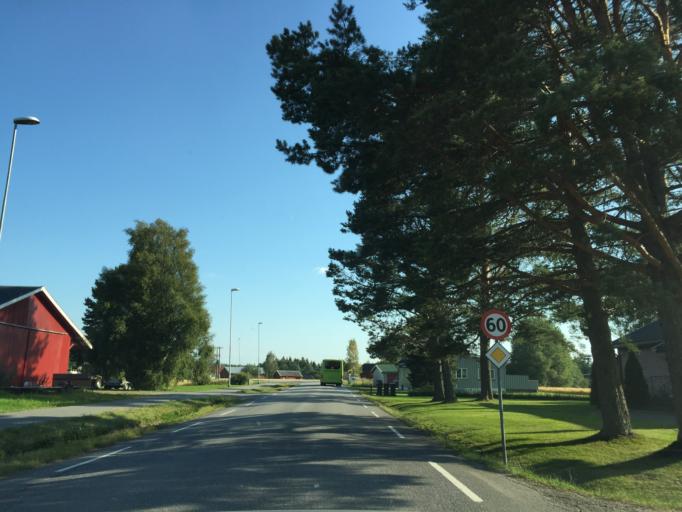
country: NO
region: Akershus
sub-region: Nes
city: Fjellfoten
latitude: 60.1051
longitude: 11.4793
